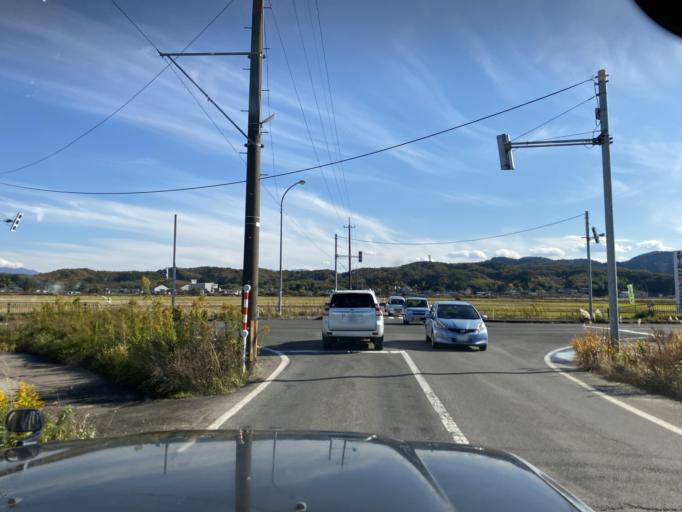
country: JP
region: Niigata
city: Niitsu-honcho
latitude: 37.7565
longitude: 139.0912
